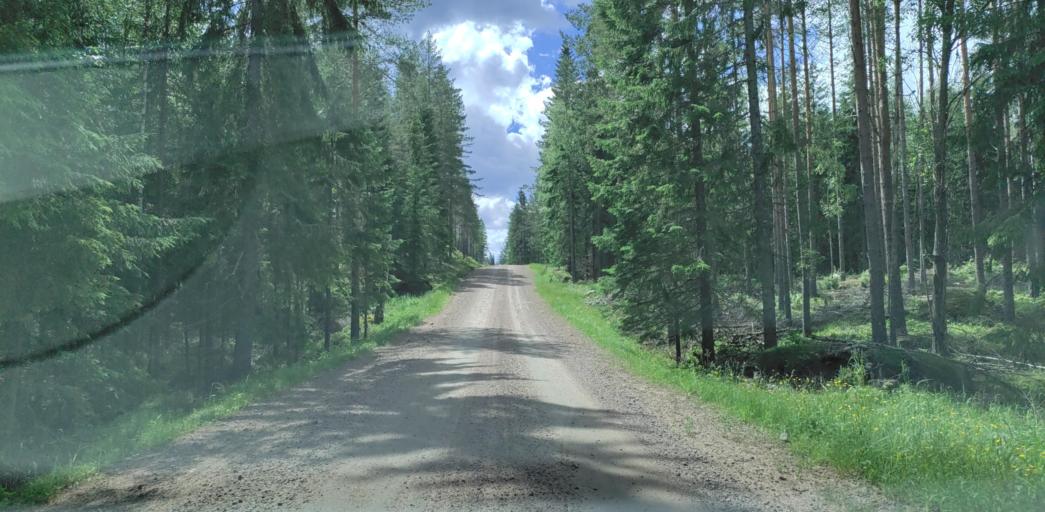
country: SE
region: Vaermland
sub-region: Hagfors Kommun
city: Ekshaerad
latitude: 60.0999
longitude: 13.3506
